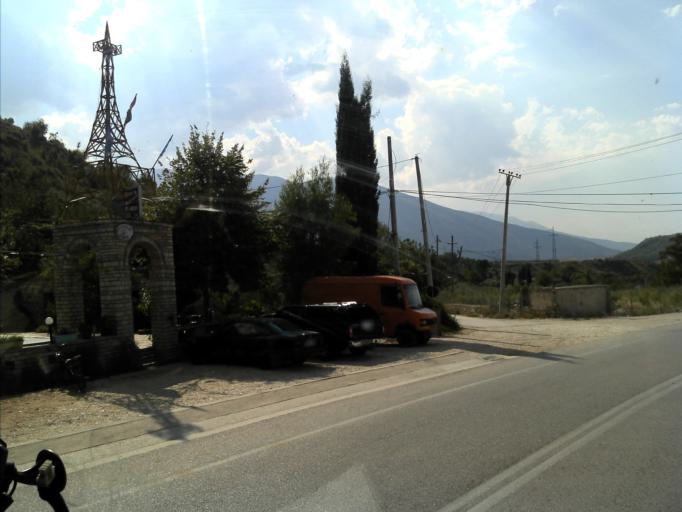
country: AL
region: Gjirokaster
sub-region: Rrethi i Tepelenes
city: Memaliaj
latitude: 40.3496
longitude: 19.9748
